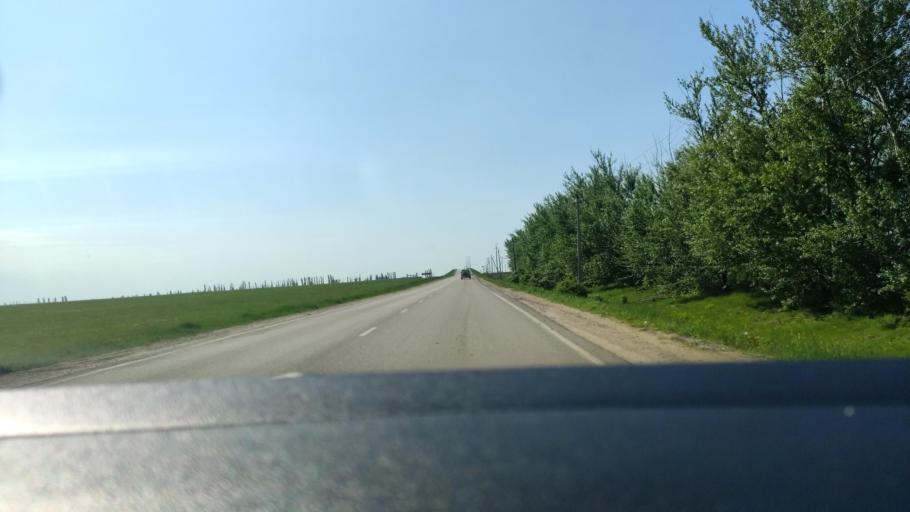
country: RU
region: Voronezj
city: Novaya Usman'
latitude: 51.5984
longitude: 39.3737
